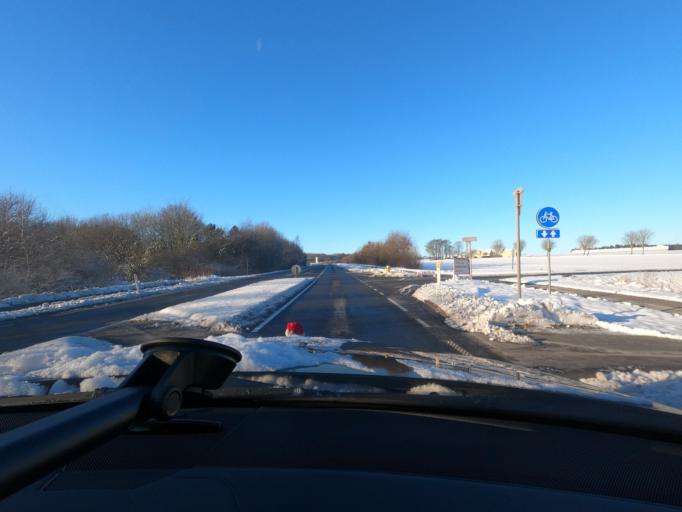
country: DK
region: South Denmark
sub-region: Tonder Kommune
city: Toftlund
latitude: 55.1350
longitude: 9.1291
